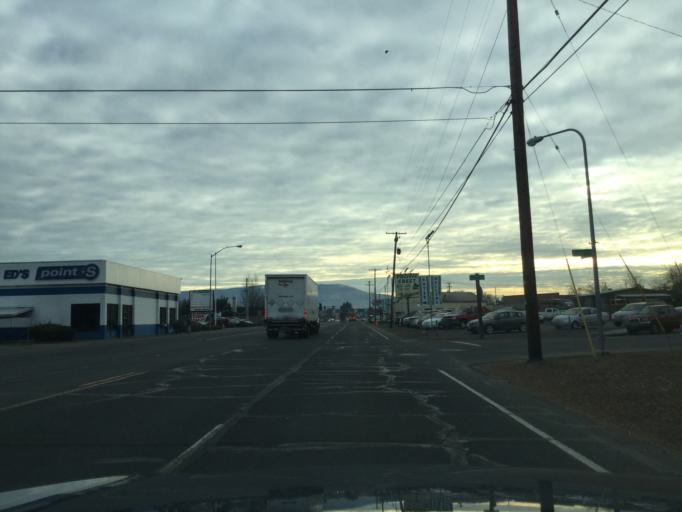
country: US
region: Oregon
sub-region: Jackson County
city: Medford
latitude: 42.3481
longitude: -122.8884
